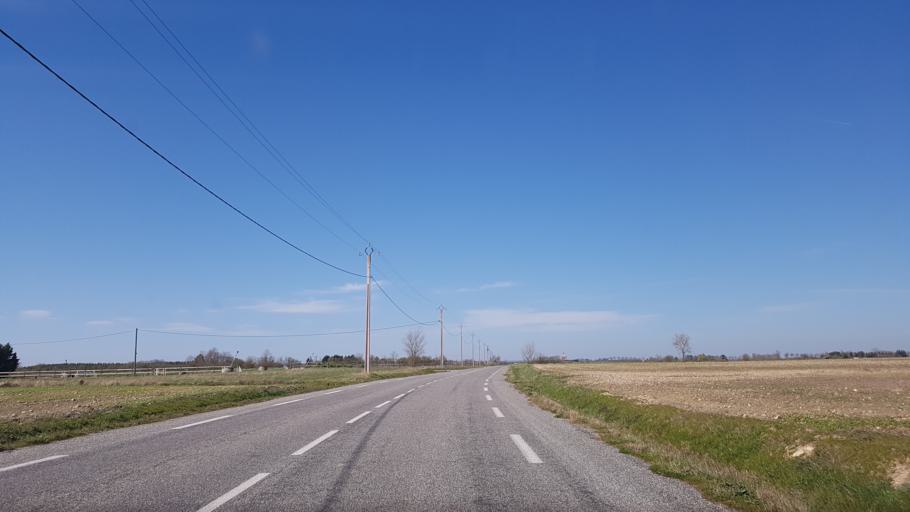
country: FR
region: Midi-Pyrenees
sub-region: Departement de l'Ariege
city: Mazeres
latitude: 43.2278
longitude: 1.6778
